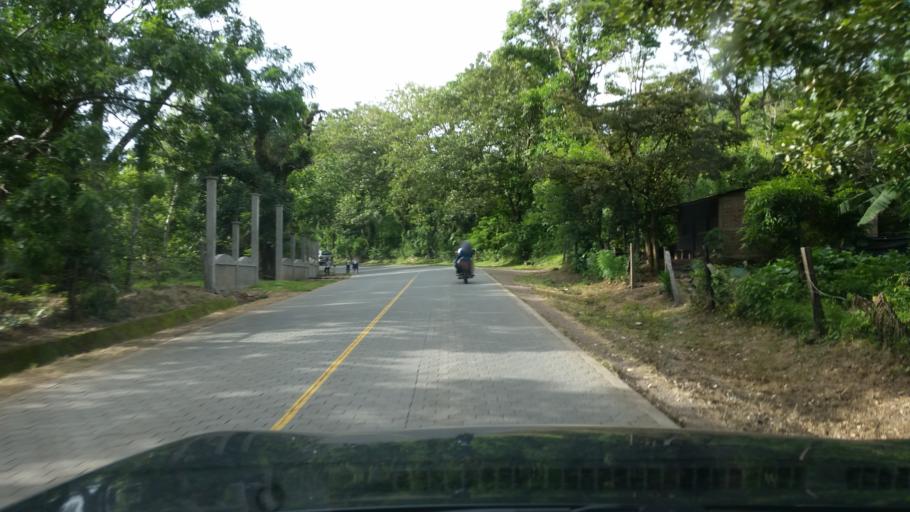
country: NI
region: Matagalpa
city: San Ramon
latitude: 13.1597
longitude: -85.7307
